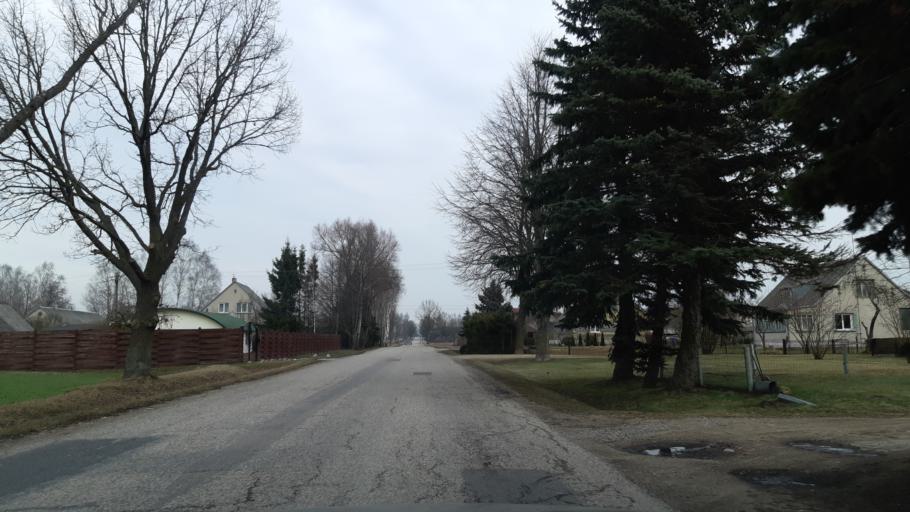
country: LT
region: Marijampoles apskritis
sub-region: Marijampole Municipality
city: Marijampole
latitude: 54.7096
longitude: 23.3147
